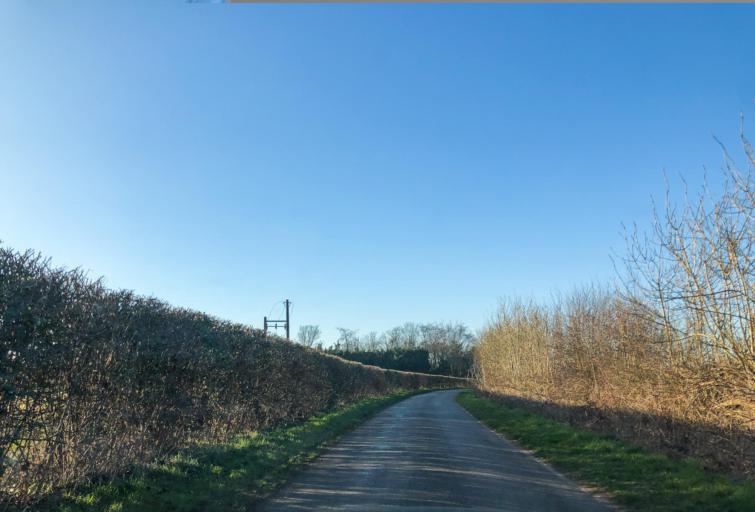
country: GB
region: England
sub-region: Warwickshire
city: Warwick
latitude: 52.2421
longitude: -1.5840
